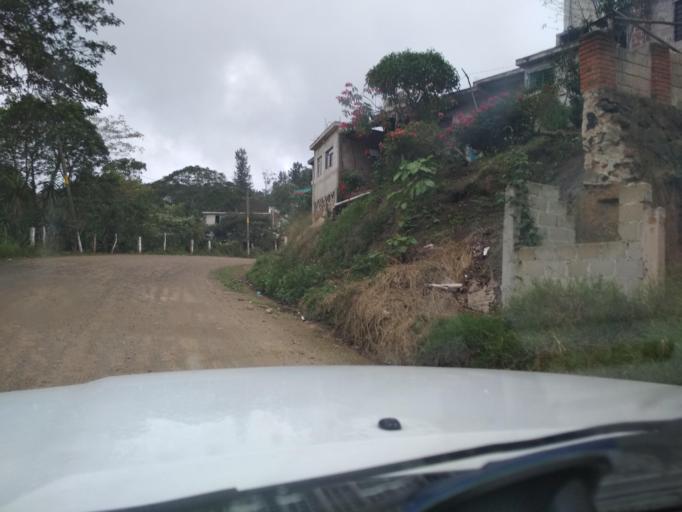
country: MX
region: Veracruz
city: El Castillo
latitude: 19.5399
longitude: -96.8296
